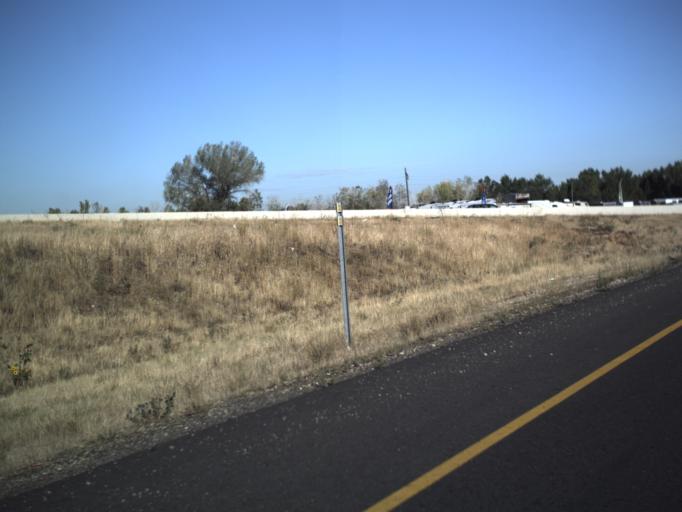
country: US
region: Utah
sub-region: Weber County
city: Marriott-Slaterville
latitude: 41.2308
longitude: -112.0123
